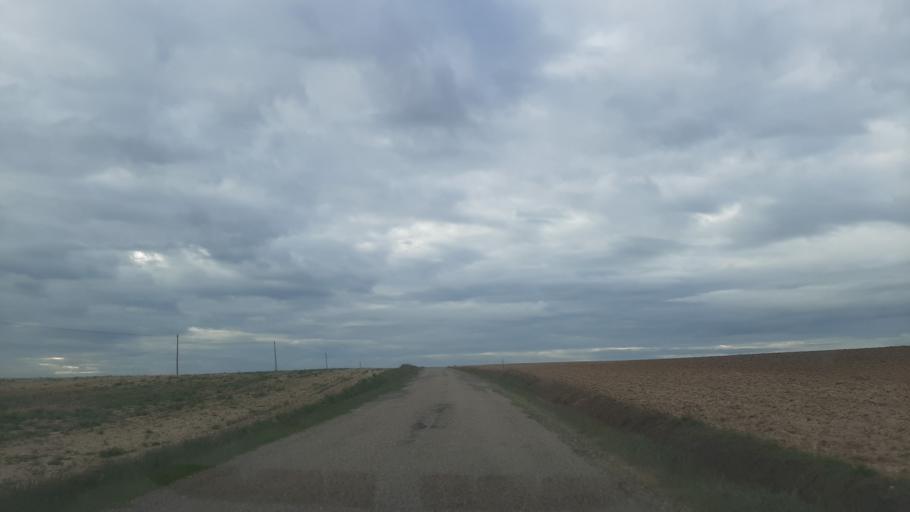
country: ES
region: Castille and Leon
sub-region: Provincia de Salamanca
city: Palaciosrubios
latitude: 41.0675
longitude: -5.2057
